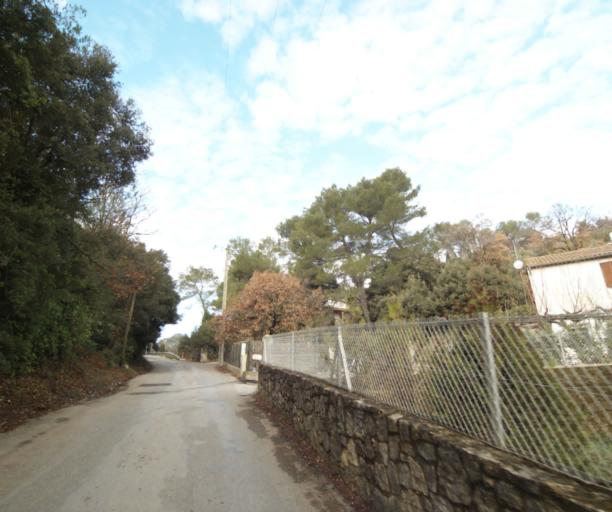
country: FR
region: Provence-Alpes-Cote d'Azur
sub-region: Departement du Var
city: Trans-en-Provence
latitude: 43.5015
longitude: 6.4800
